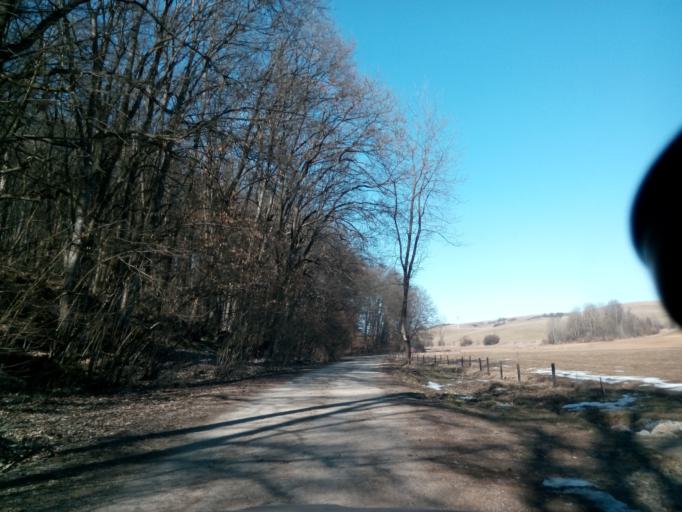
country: SK
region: Kosicky
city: Roznava
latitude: 48.5457
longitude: 20.5474
